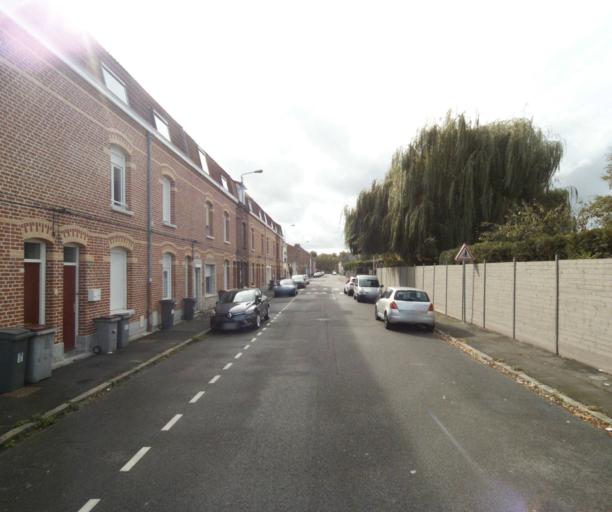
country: FR
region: Nord-Pas-de-Calais
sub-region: Departement du Nord
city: Houplines
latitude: 50.6846
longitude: 2.9004
